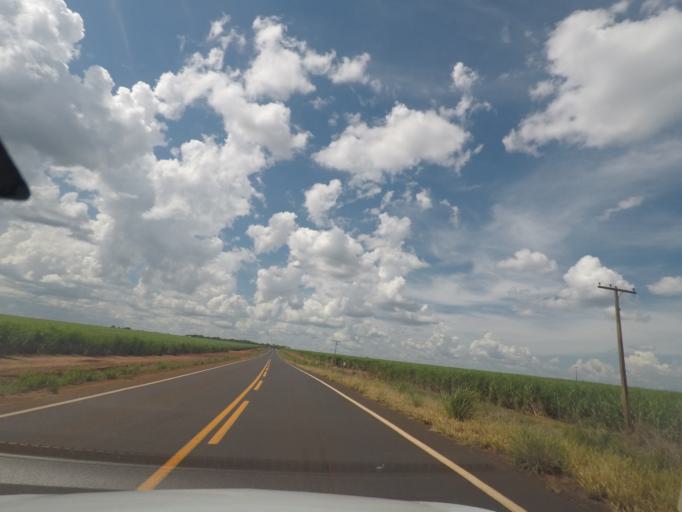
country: BR
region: Minas Gerais
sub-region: Conceicao Das Alagoas
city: Conceicao das Alagoas
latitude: -19.8594
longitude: -48.6008
